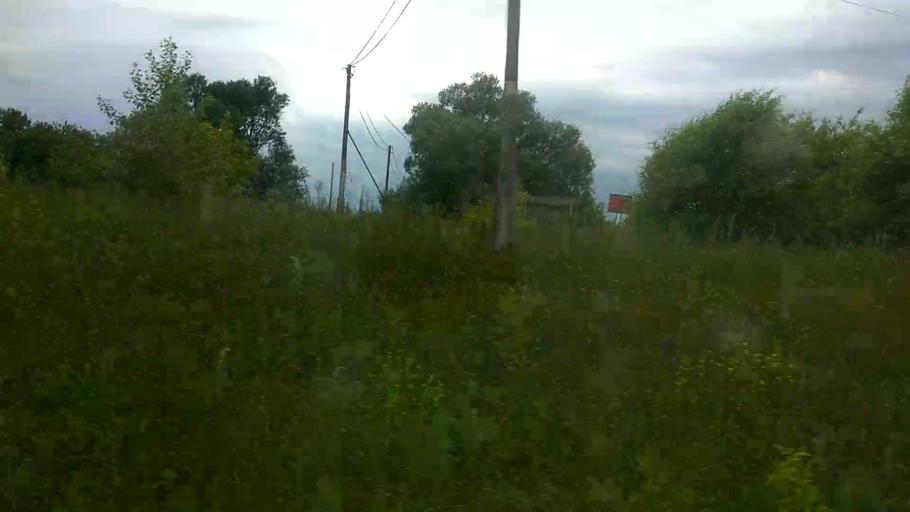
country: RU
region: Moskovskaya
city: Ozery
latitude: 54.8366
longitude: 38.5825
